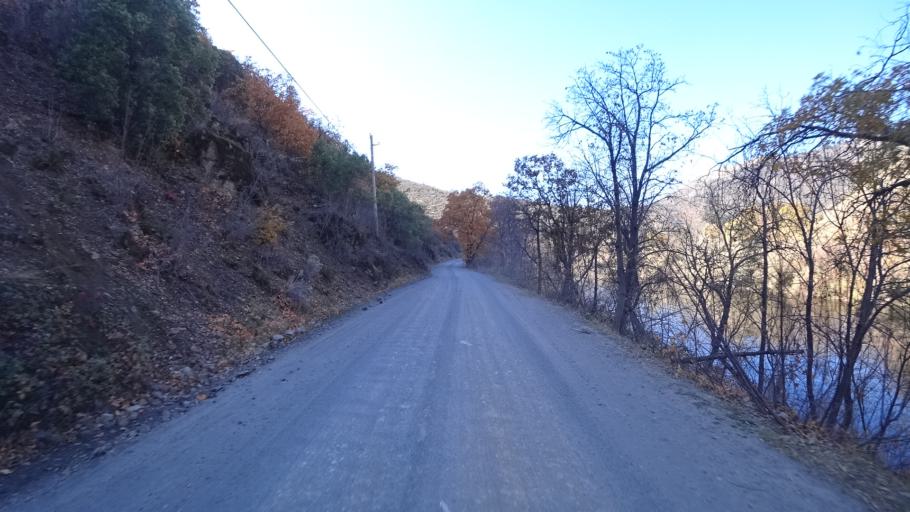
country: US
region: California
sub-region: Siskiyou County
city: Yreka
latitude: 41.8311
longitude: -122.6285
